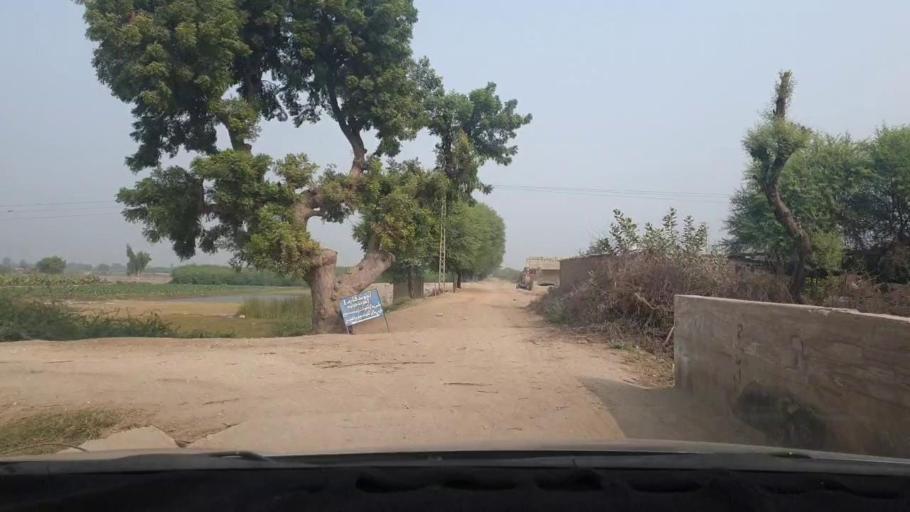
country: PK
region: Sindh
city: Matiari
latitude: 25.6445
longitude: 68.5601
